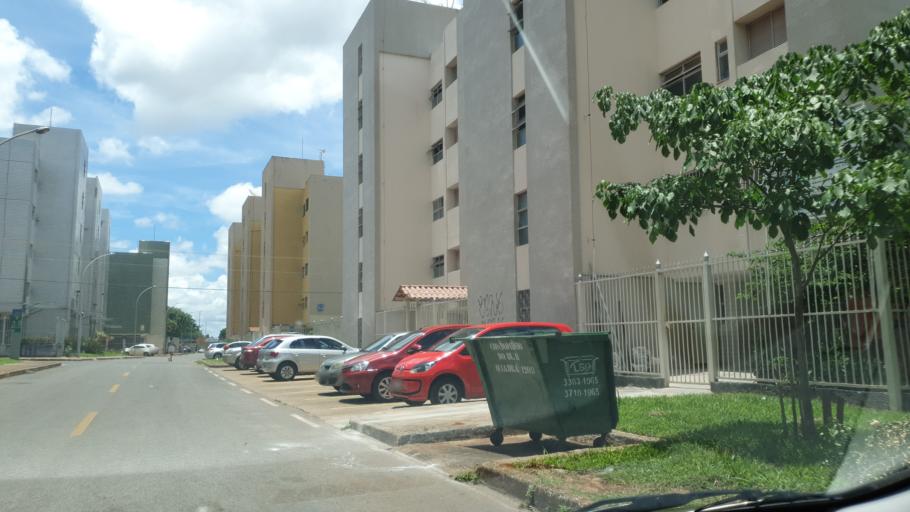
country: BR
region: Federal District
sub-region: Brasilia
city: Brasilia
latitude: -15.7925
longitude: -47.9352
